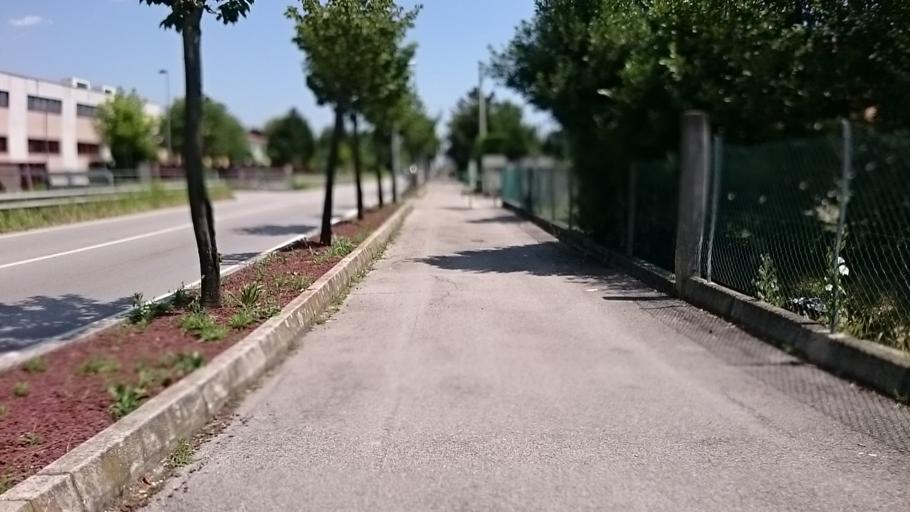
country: IT
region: Veneto
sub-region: Provincia di Padova
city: Villanova
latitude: 45.4891
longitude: 11.9758
